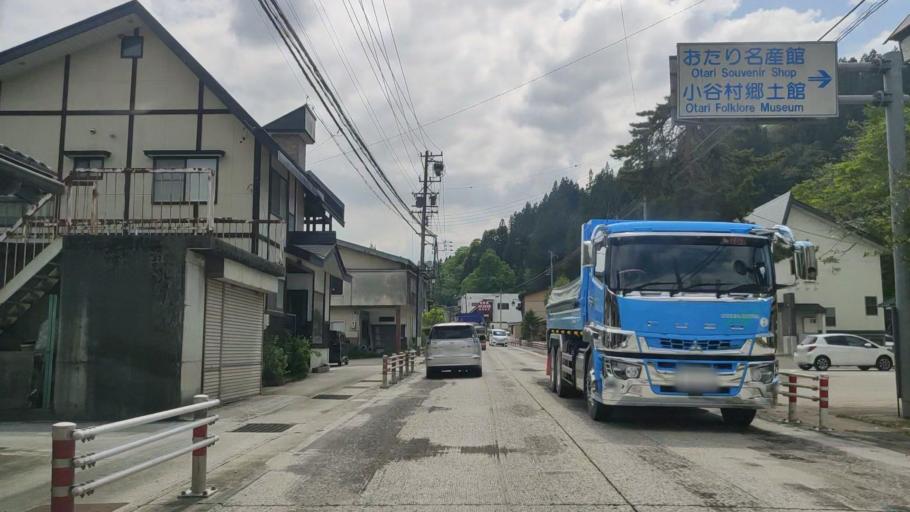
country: JP
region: Nagano
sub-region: Kitaazumi Gun
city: Hakuba
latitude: 36.7785
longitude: 137.9096
